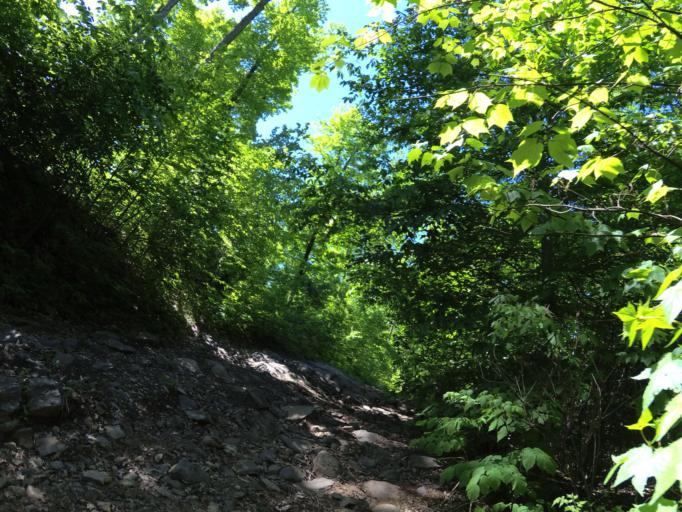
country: CA
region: Ontario
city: Renfrew
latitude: 45.0667
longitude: -77.0734
